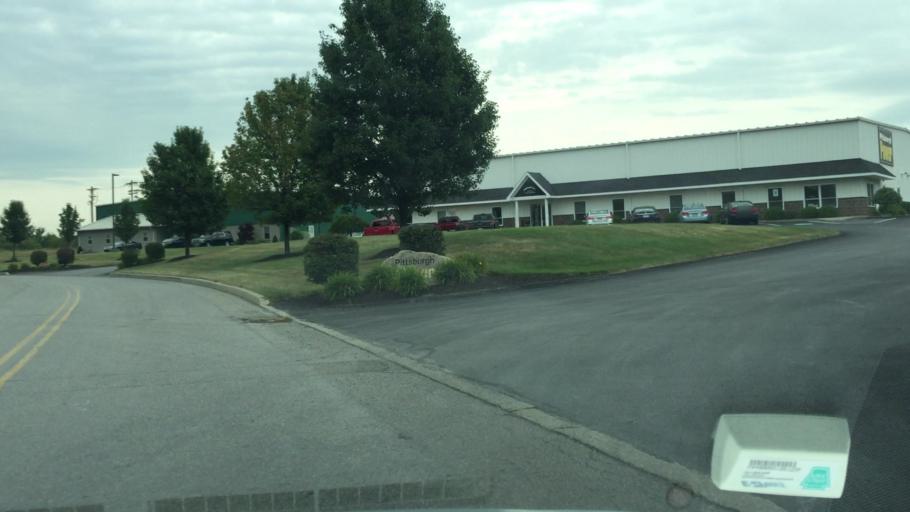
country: US
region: Pennsylvania
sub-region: Butler County
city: Saxonburg
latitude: 40.7332
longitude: -79.8452
